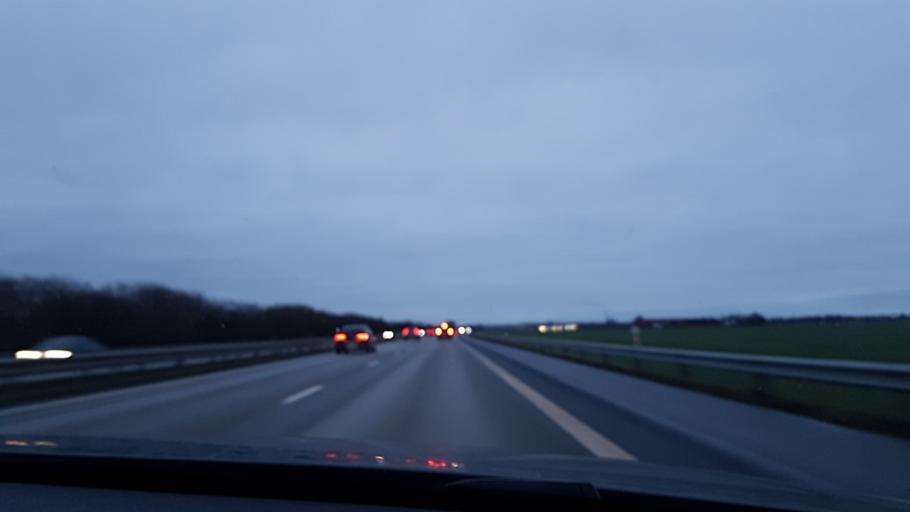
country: SE
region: Skane
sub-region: Lomma Kommun
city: Lomma
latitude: 55.7100
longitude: 13.0953
